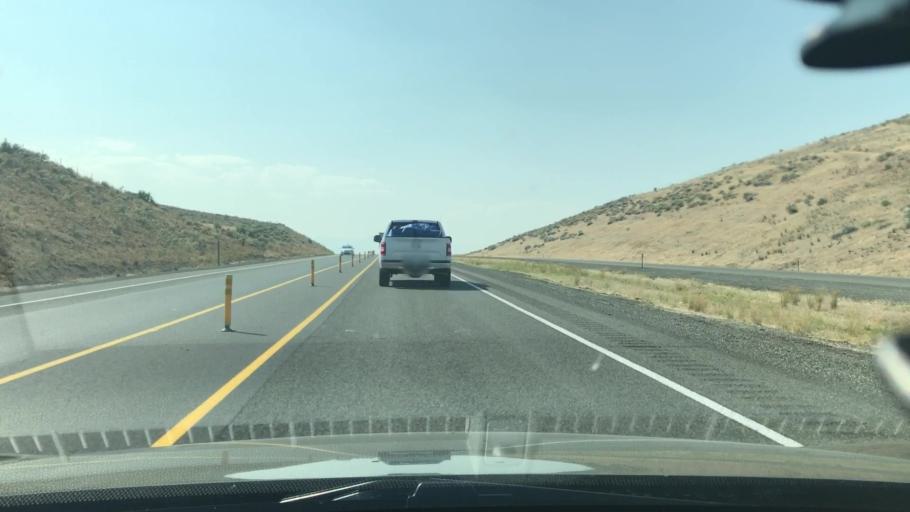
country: US
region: Oregon
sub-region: Baker County
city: Baker City
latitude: 44.6835
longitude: -117.6612
